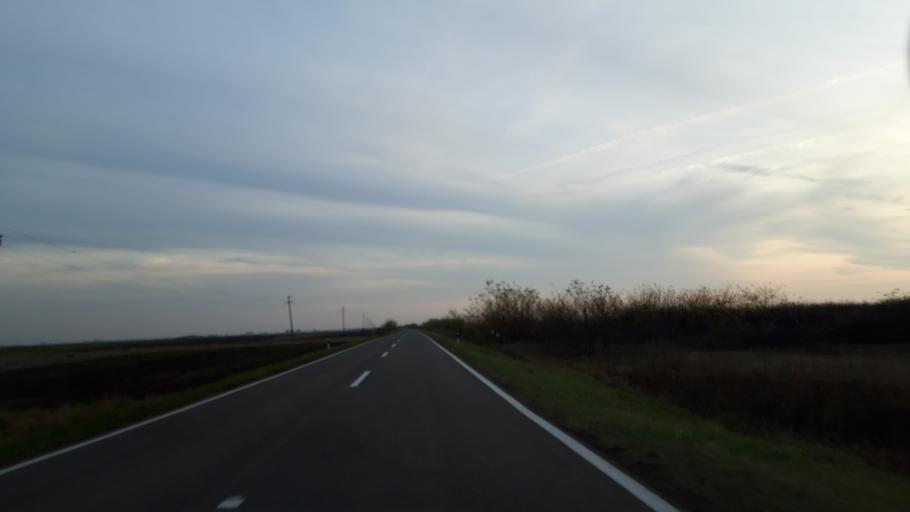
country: RS
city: Ostojicevo
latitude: 45.8662
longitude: 20.1648
